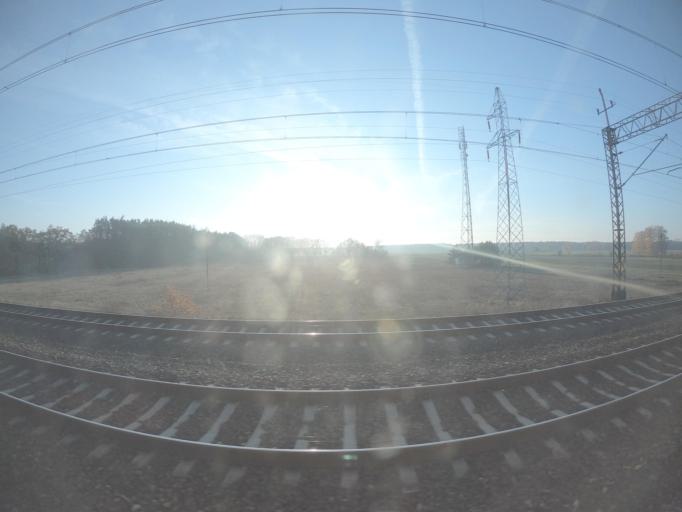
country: PL
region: Lubusz
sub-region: Powiat slubicki
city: Rzepin
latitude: 52.3239
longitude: 14.8467
